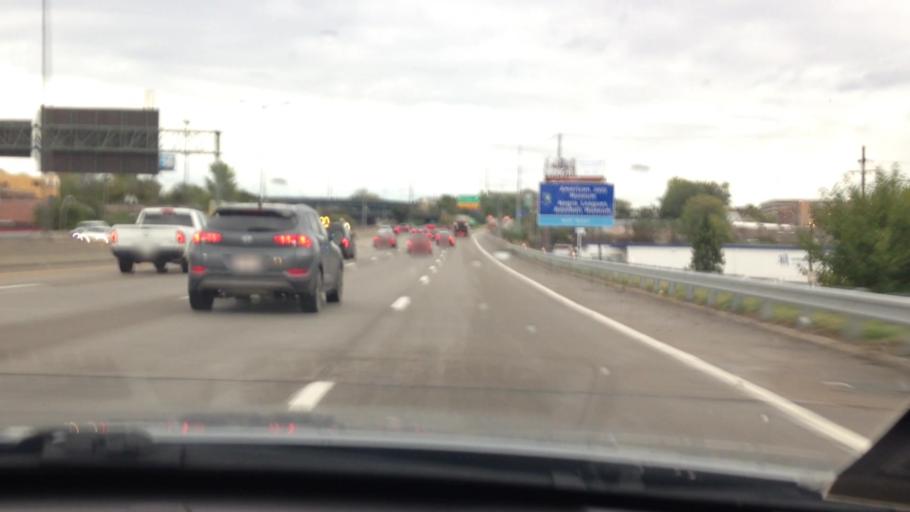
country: US
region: Missouri
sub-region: Jackson County
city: Kansas City
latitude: 39.0911
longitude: -94.5718
